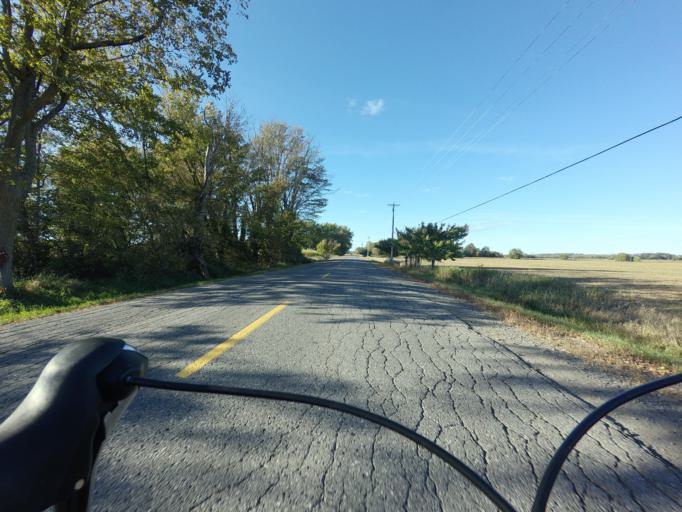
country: CA
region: Ontario
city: Bells Corners
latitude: 45.2122
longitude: -75.7972
